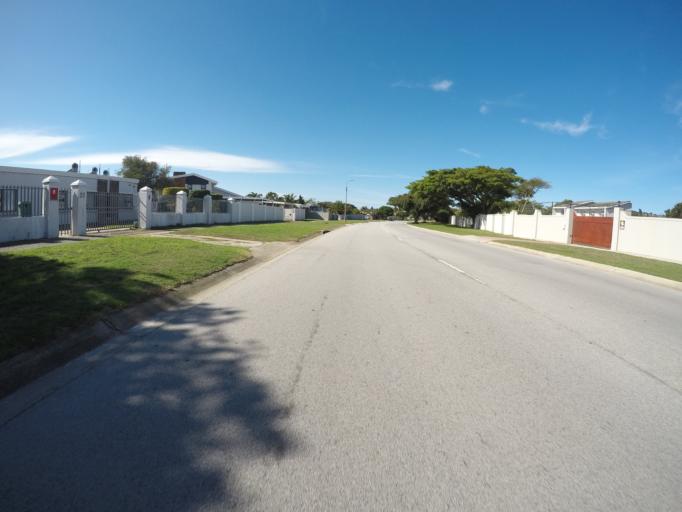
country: ZA
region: Eastern Cape
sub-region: Nelson Mandela Bay Metropolitan Municipality
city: Port Elizabeth
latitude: -33.9929
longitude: 25.6612
